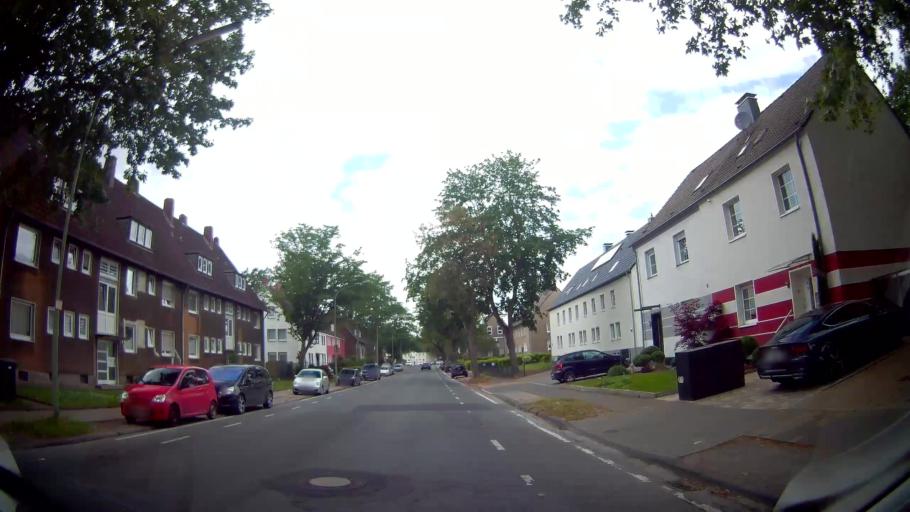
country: DE
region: North Rhine-Westphalia
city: Bochum-Hordel
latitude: 51.5239
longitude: 7.1747
